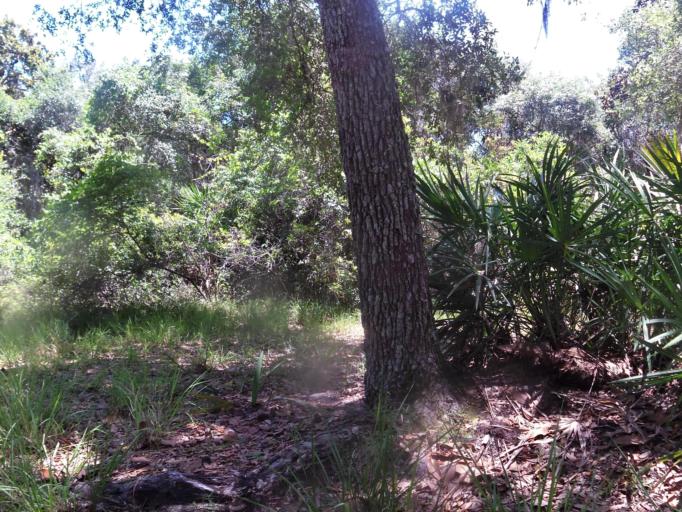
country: US
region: Florida
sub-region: Saint Johns County
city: Villano Beach
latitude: 30.0339
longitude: -81.3383
